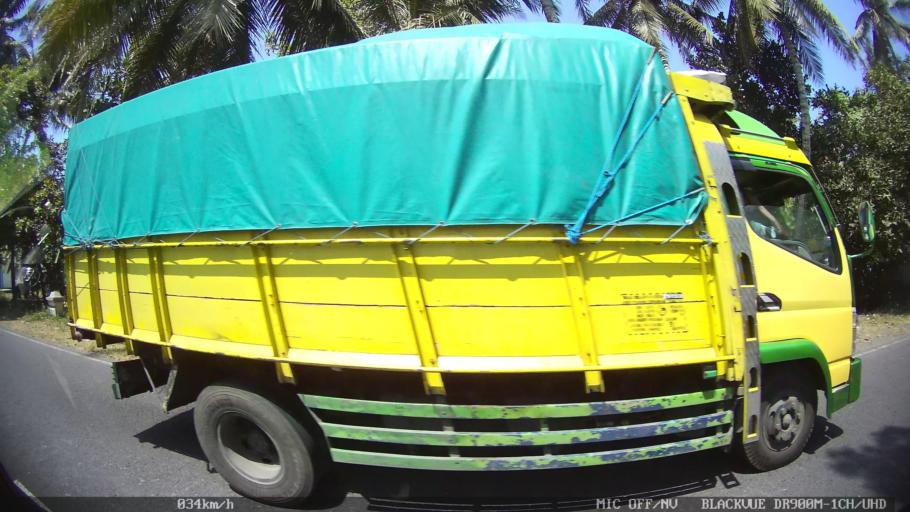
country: ID
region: Daerah Istimewa Yogyakarta
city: Srandakan
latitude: -7.9372
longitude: 110.1532
